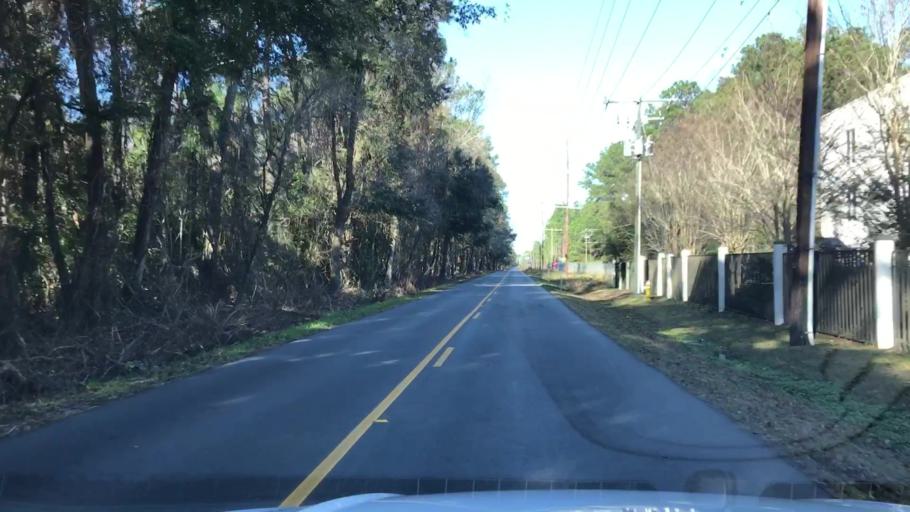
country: US
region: South Carolina
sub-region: Berkeley County
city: Ladson
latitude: 32.9867
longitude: -80.1116
